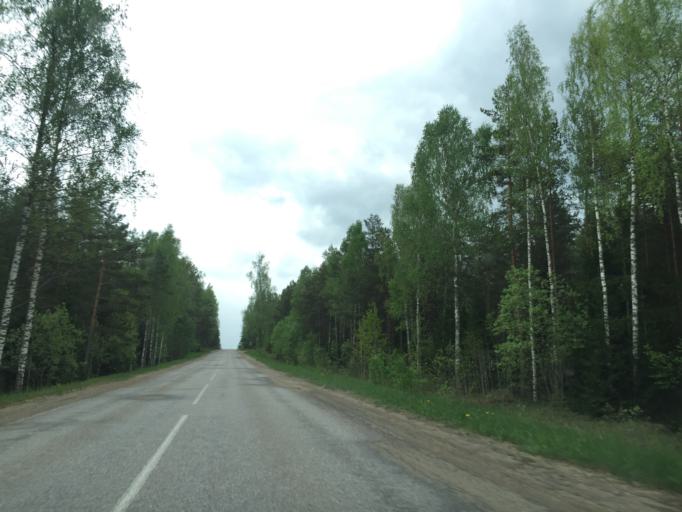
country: LV
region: Ogre
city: Ogre
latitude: 56.8468
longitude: 24.5720
